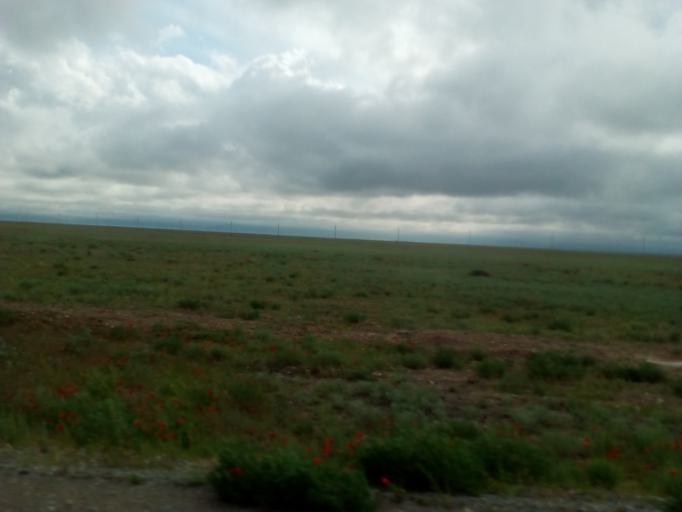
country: KZ
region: Ongtustik Qazaqstan
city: Sholaqqkorghan
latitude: 43.7432
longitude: 69.2021
